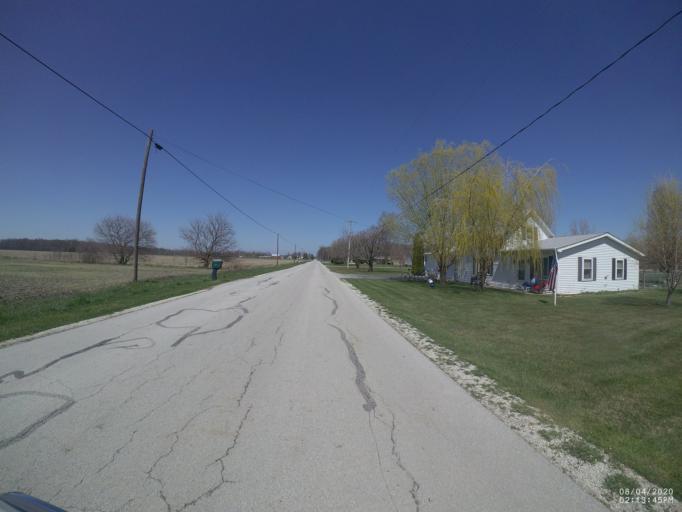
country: US
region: Ohio
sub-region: Sandusky County
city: Gibsonburg
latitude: 41.2649
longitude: -83.2644
